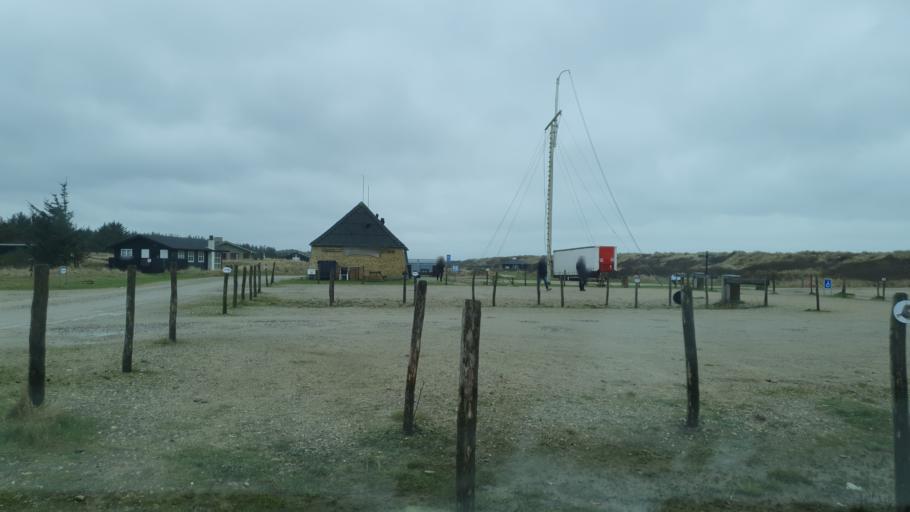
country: DK
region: North Denmark
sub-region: Jammerbugt Kommune
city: Fjerritslev
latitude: 57.1390
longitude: 9.1258
